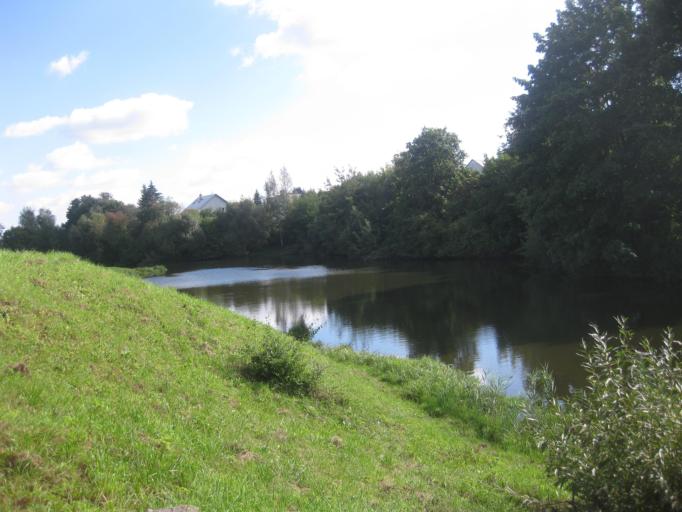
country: LT
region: Kauno apskritis
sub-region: Kauno rajonas
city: Garliava
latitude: 54.8299
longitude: 23.8785
